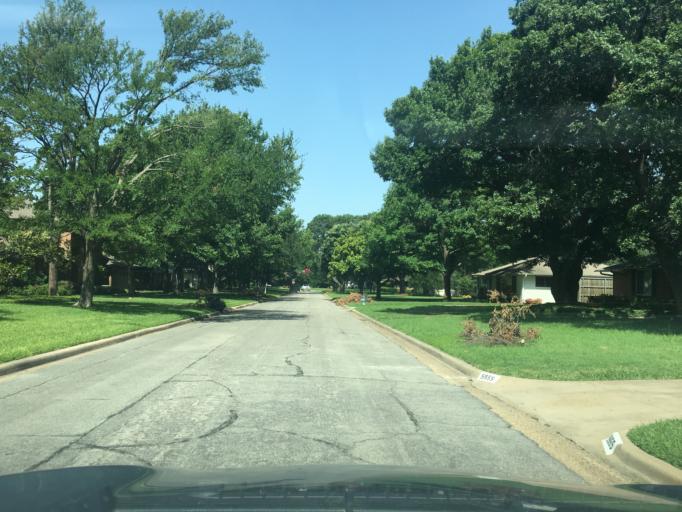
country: US
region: Texas
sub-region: Dallas County
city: University Park
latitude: 32.8995
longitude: -96.8048
